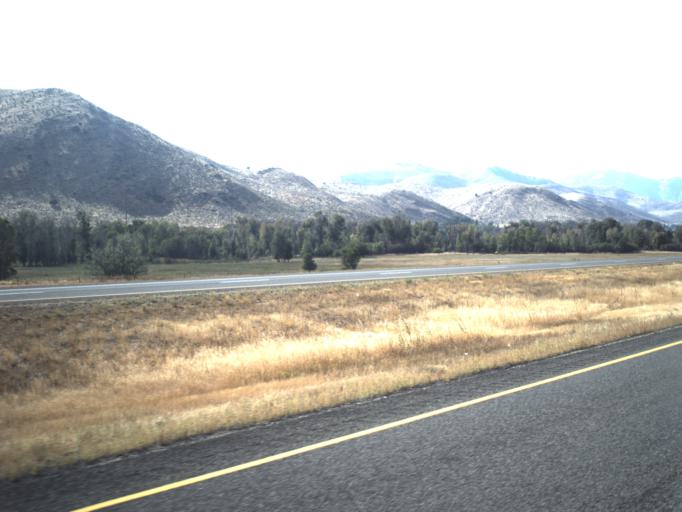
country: US
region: Utah
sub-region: Summit County
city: Coalville
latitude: 40.9904
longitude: -111.4559
